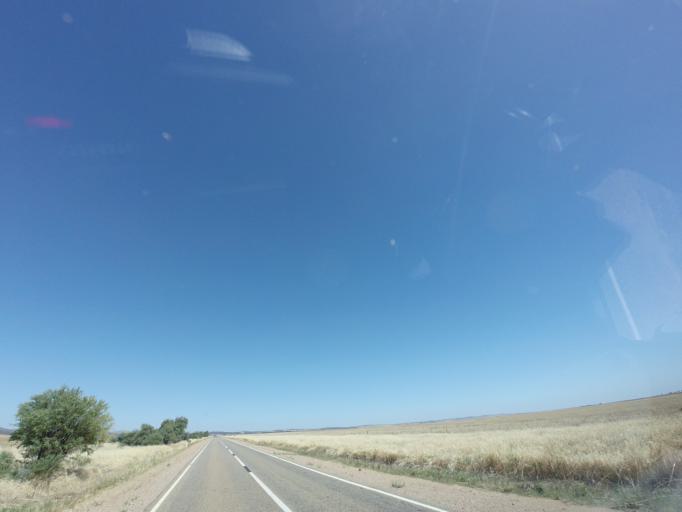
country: AU
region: South Australia
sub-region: Peterborough
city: Peterborough
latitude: -32.8263
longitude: 138.7037
